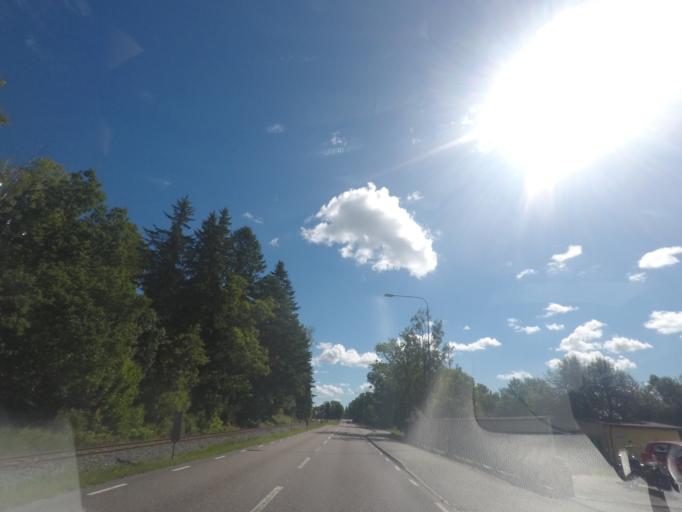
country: SE
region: Stockholm
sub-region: Norrtalje Kommun
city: Nykvarn
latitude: 59.8766
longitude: 18.0378
